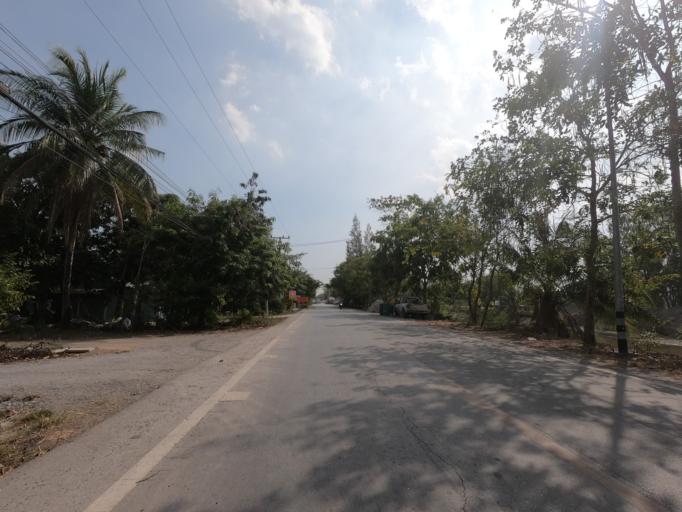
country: TH
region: Pathum Thani
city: Nong Suea
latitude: 14.1158
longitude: 100.8465
